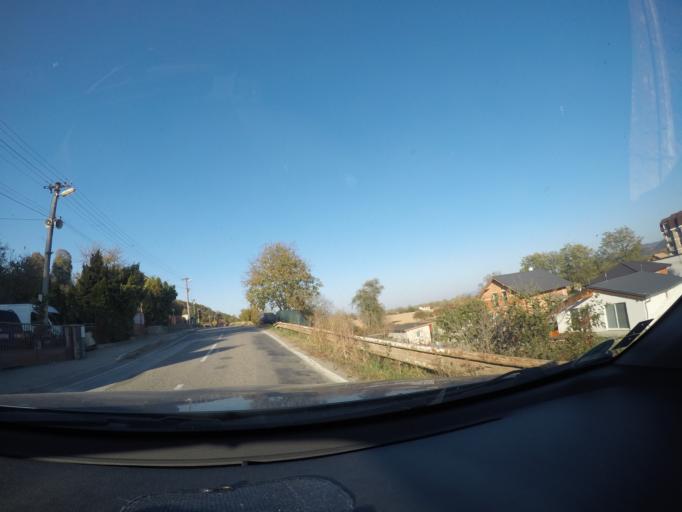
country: SK
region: Trenciansky
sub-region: Okres Trencin
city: Trencin
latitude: 48.9304
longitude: 18.0724
